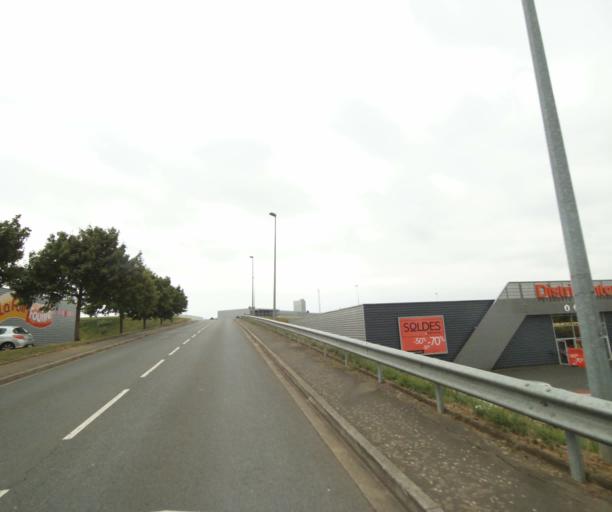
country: FR
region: Pays de la Loire
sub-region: Departement de la Sarthe
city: Solesmes
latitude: 47.8364
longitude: -0.2995
